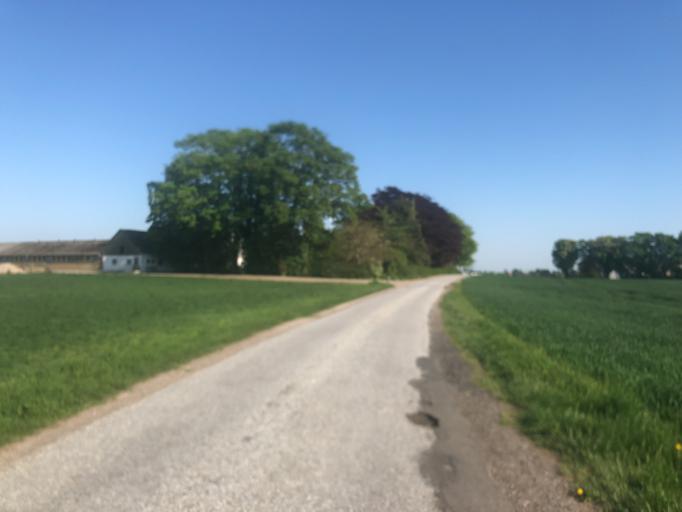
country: DK
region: Zealand
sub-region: Ringsted Kommune
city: Ringsted
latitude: 55.4780
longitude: 11.7977
